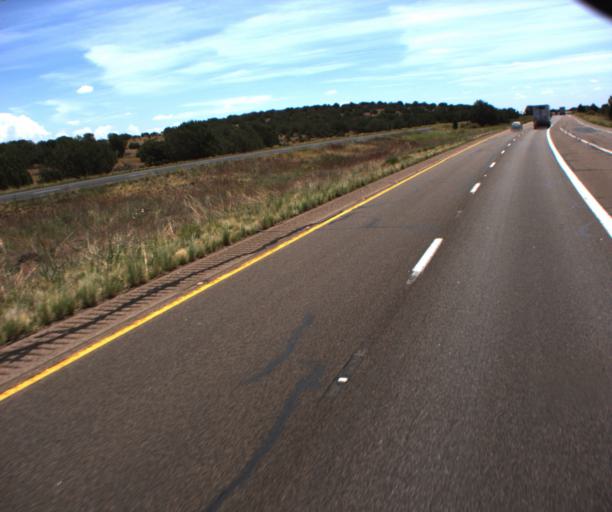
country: US
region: Arizona
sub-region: Yavapai County
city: Paulden
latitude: 35.2681
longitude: -112.7276
